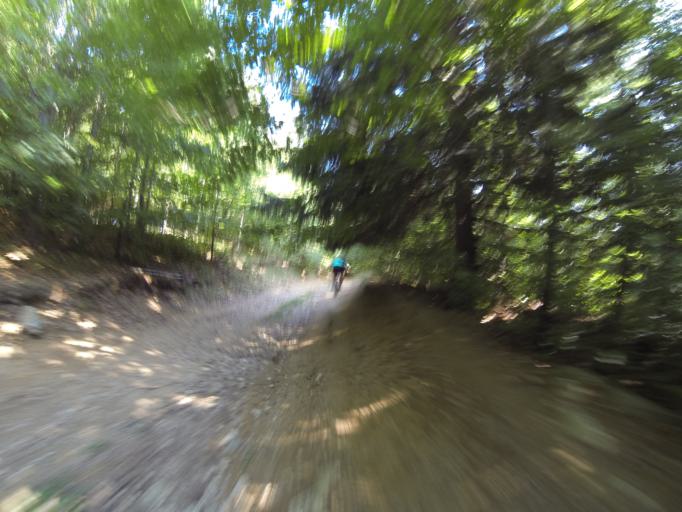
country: RO
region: Valcea
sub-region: Comuna Vaideeni
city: Vaideeni
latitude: 45.2324
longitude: 23.9631
